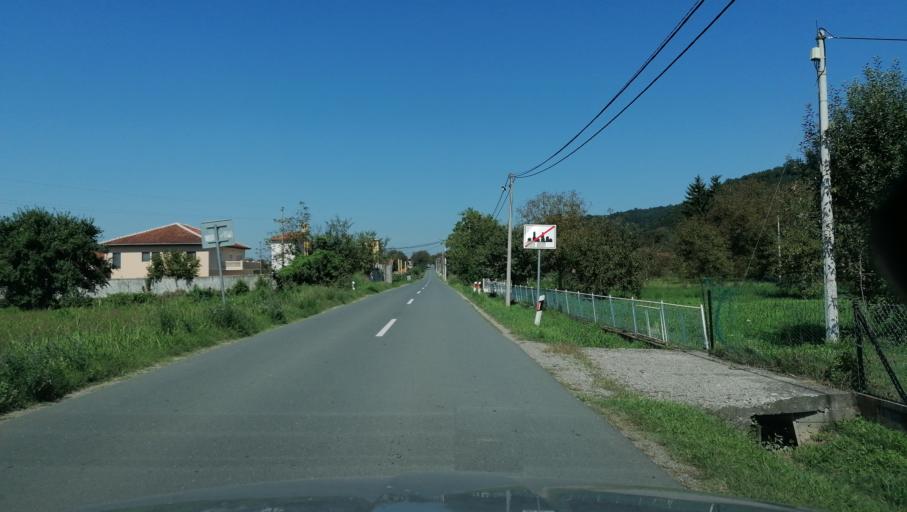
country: RS
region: Central Serbia
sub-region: Raski Okrug
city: Vrnjacka Banja
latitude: 43.6706
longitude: 20.9069
